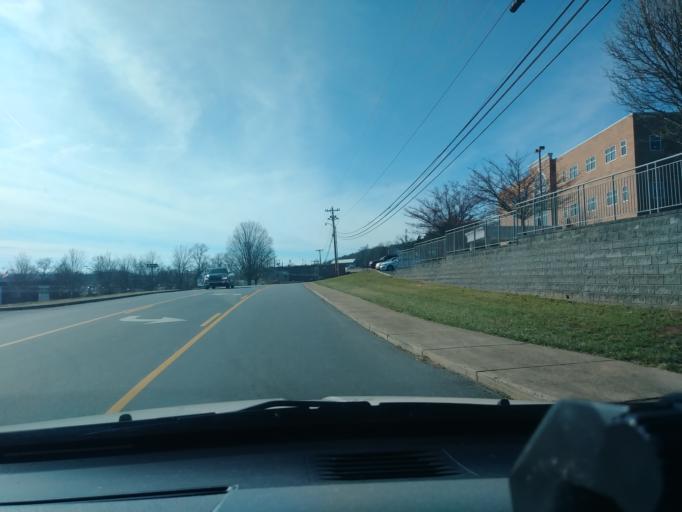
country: US
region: Tennessee
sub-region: Greene County
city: Greeneville
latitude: 36.1503
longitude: -82.8443
